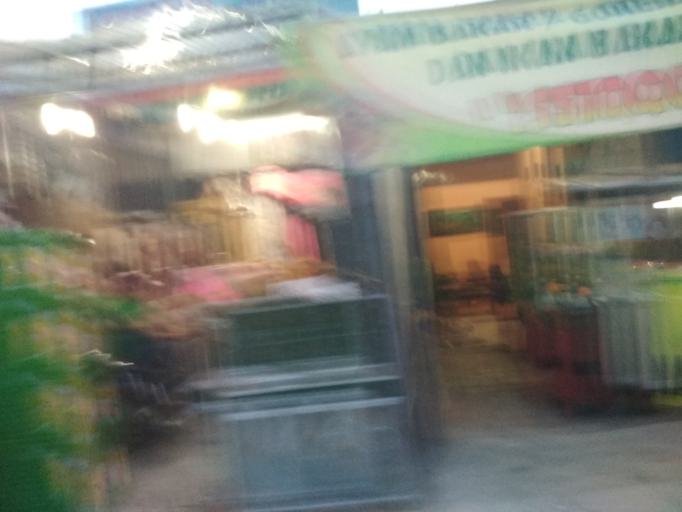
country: ID
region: West Java
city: Caringin
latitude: -6.7096
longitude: 106.8224
